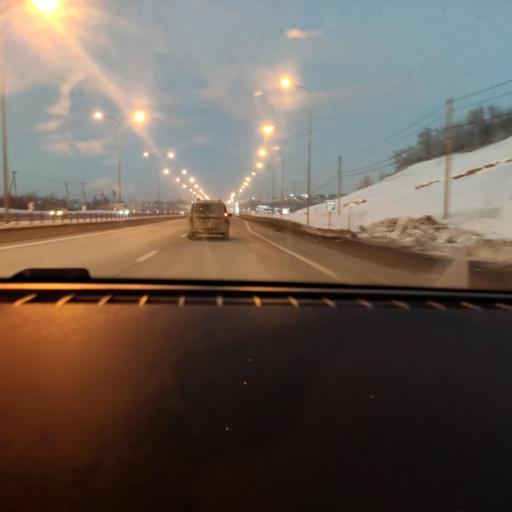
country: RU
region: Samara
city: Novosemeykino
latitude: 53.3979
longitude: 50.3277
